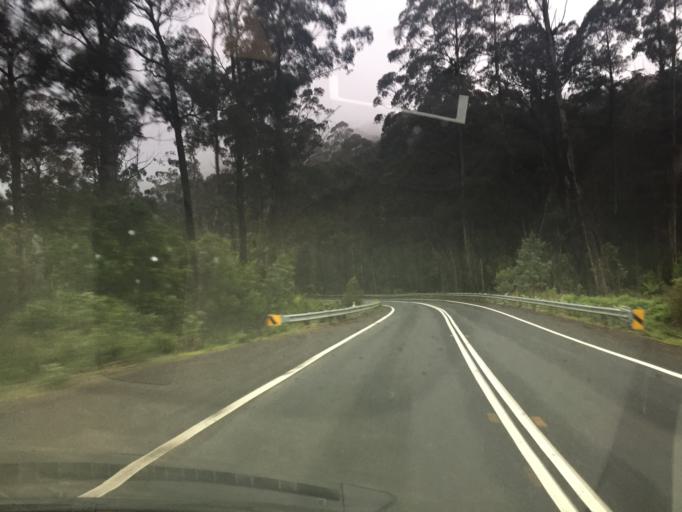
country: AU
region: New South Wales
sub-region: Bombala
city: Bombala
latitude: -36.6019
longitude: 149.4392
